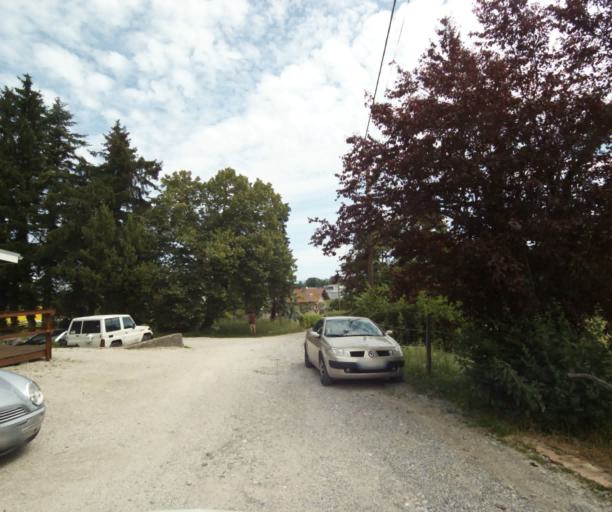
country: FR
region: Rhone-Alpes
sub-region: Departement de la Haute-Savoie
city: Margencel
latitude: 46.3465
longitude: 6.4377
